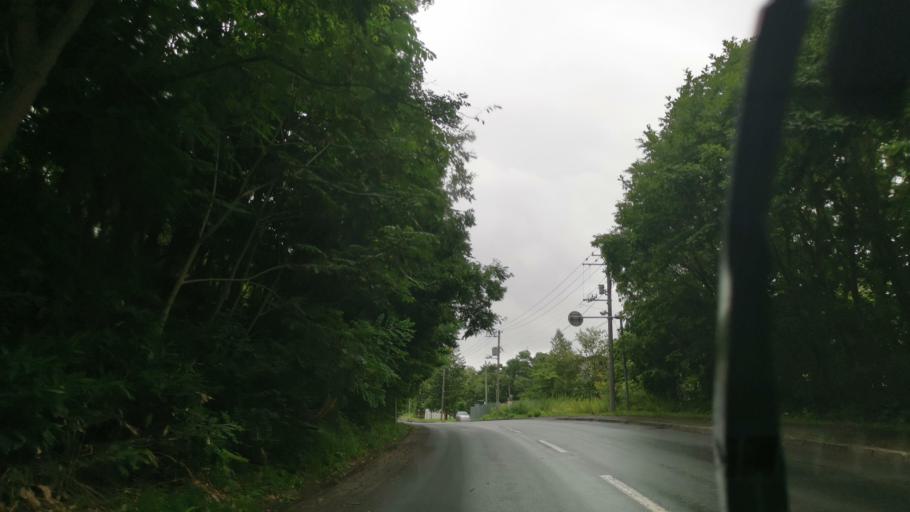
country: JP
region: Hokkaido
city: Sapporo
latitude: 42.9693
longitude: 141.3596
